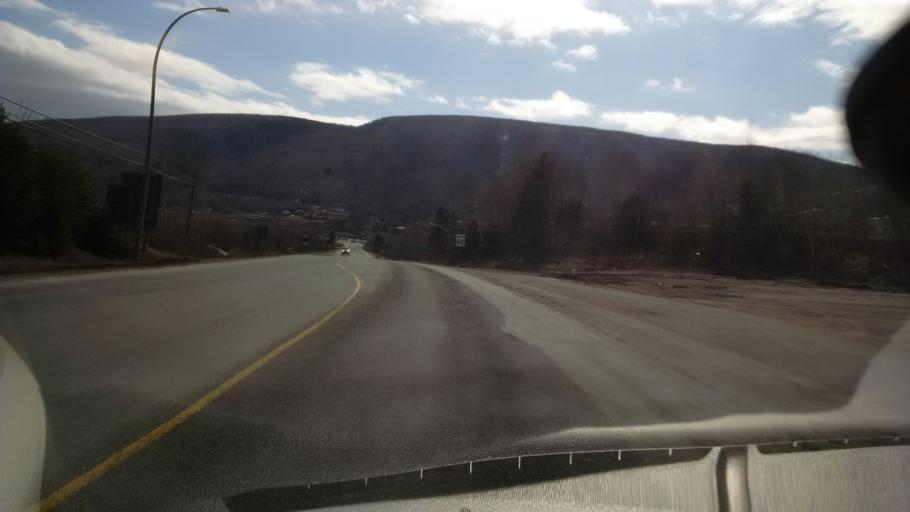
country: CA
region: Nova Scotia
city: Princeville
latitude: 45.9741
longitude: -61.1281
